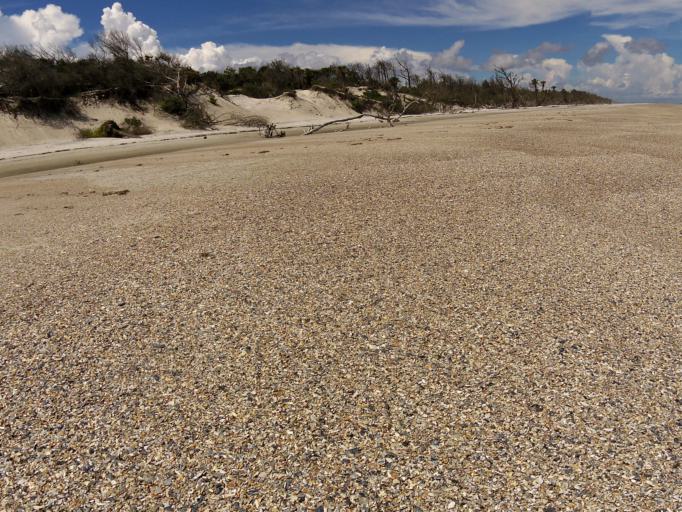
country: US
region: Florida
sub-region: Duval County
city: Atlantic Beach
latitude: 30.4763
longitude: -81.4134
